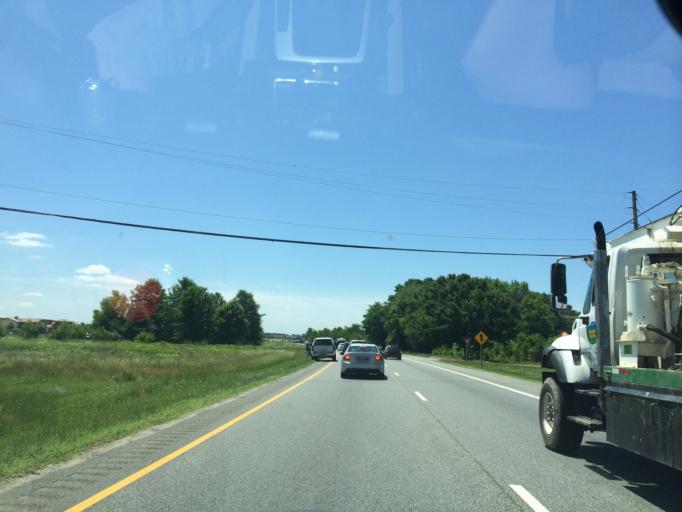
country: US
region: Maryland
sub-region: Talbot County
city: Easton
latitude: 38.7991
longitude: -76.0608
